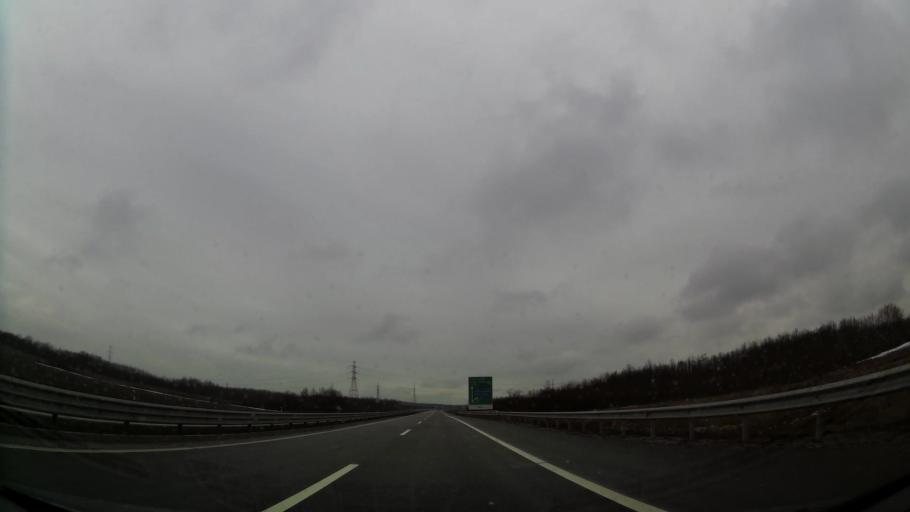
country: XK
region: Ferizaj
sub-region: Komuna e Ferizajt
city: Ferizaj
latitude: 42.3798
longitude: 21.2037
